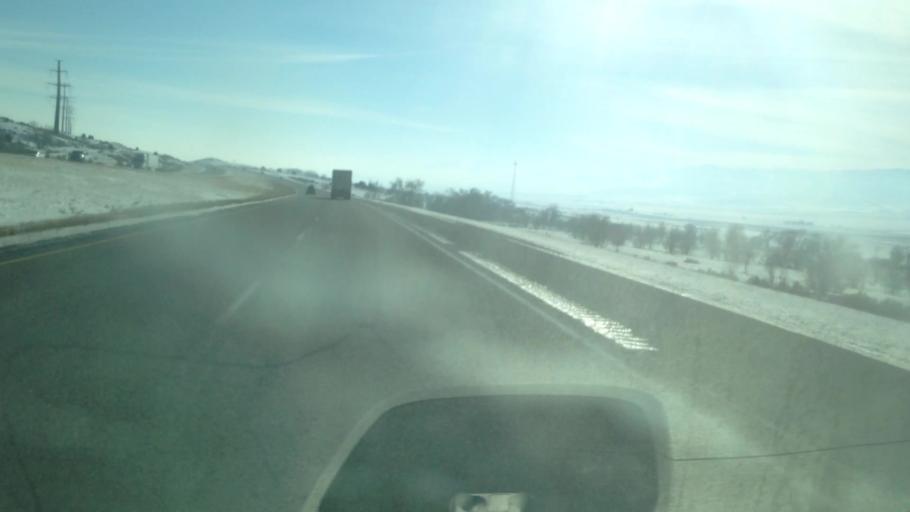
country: US
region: Idaho
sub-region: Oneida County
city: Malad City
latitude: 42.0623
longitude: -112.2192
